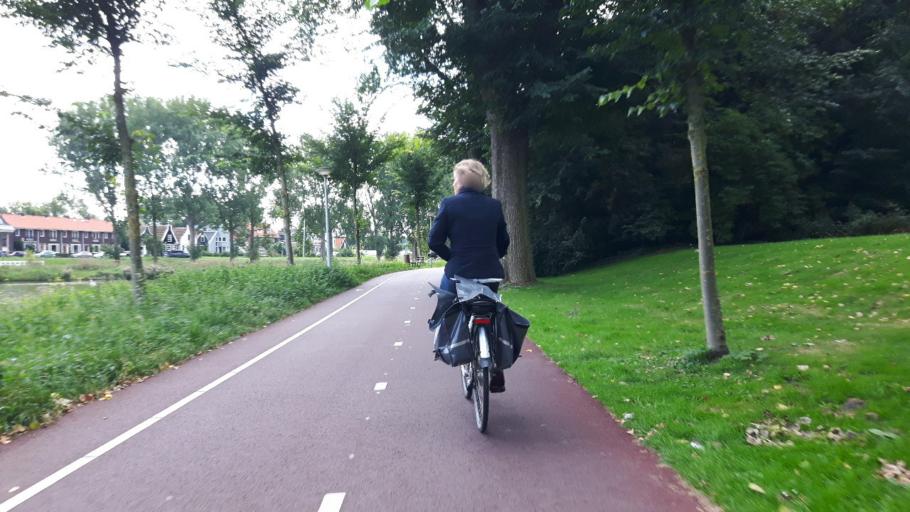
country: NL
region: North Holland
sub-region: Gemeente Landsmeer
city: Landsmeer
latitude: 52.3973
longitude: 4.9212
